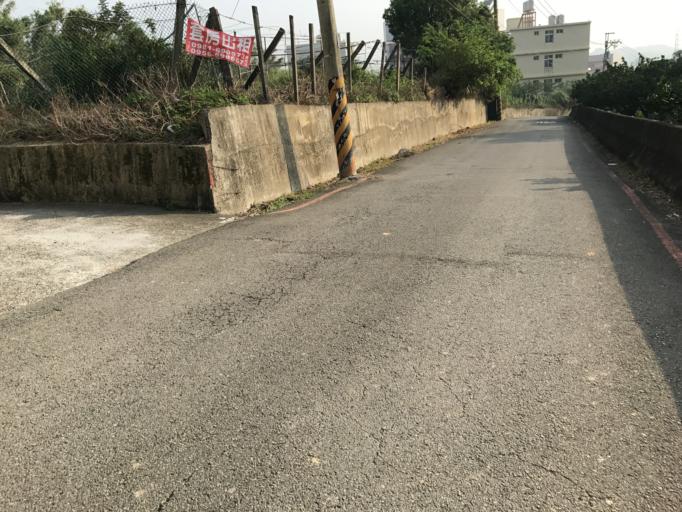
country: TW
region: Taiwan
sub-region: Hsinchu
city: Hsinchu
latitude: 24.7572
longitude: 120.9506
